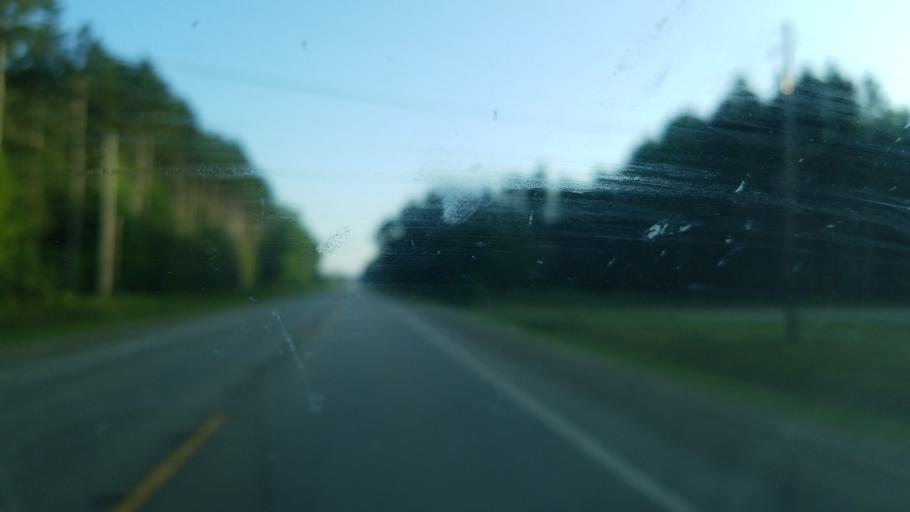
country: US
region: Michigan
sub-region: Montcalm County
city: Stanton
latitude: 43.2660
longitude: -85.0737
